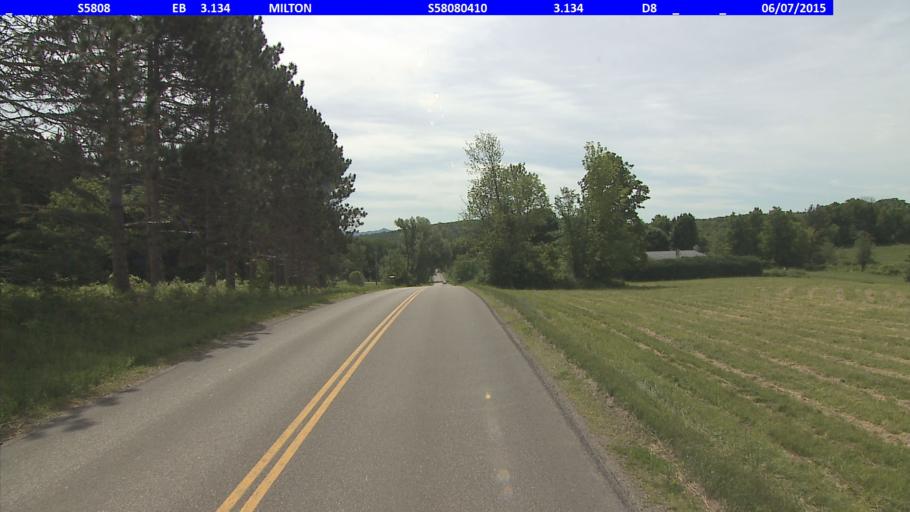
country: US
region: Vermont
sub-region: Chittenden County
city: Milton
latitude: 44.6412
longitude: -73.0573
